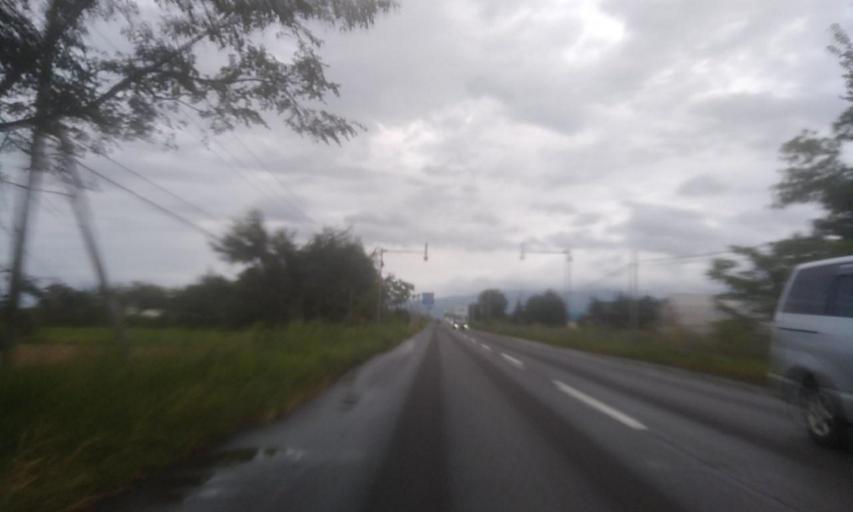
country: JP
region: Hokkaido
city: Abashiri
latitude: 43.8994
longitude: 144.6332
